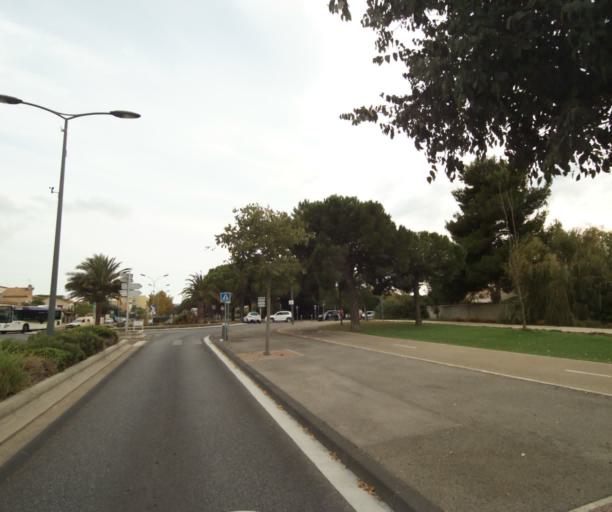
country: FR
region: Provence-Alpes-Cote d'Azur
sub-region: Departement des Bouches-du-Rhone
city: Marignane
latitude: 43.4158
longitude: 5.2039
